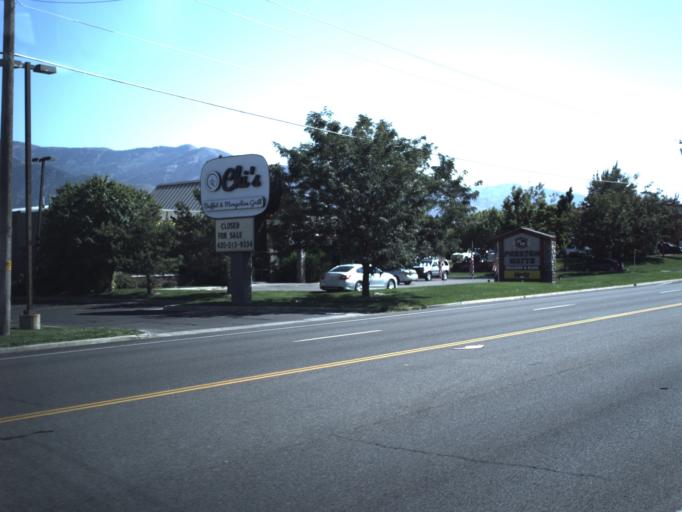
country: US
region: Utah
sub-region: Cache County
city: North Logan
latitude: 41.7697
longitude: -111.8342
